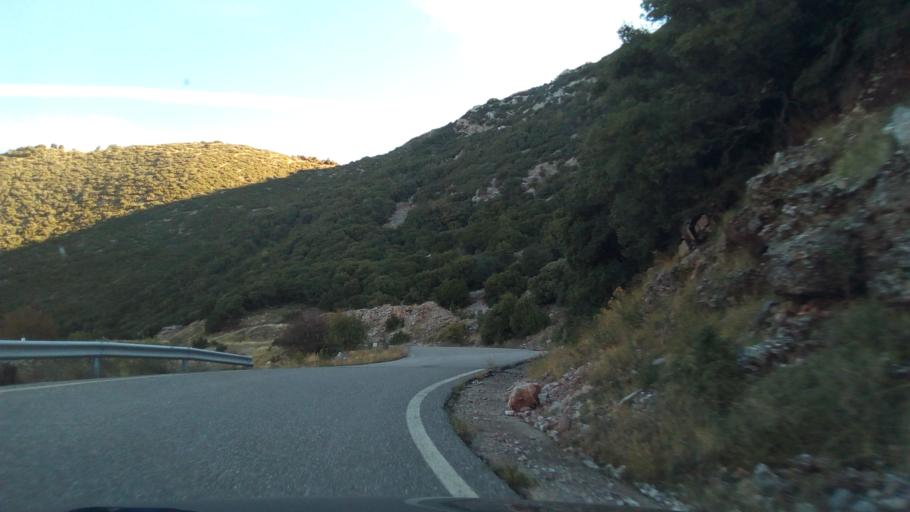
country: GR
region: West Greece
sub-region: Nomos Aitolias kai Akarnanias
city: Nafpaktos
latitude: 38.4891
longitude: 21.8570
